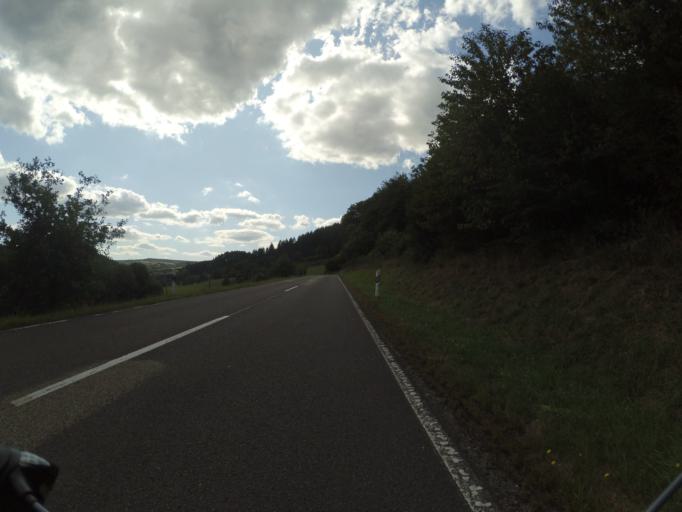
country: DE
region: Rheinland-Pfalz
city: Budlich
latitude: 49.7785
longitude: 6.8945
